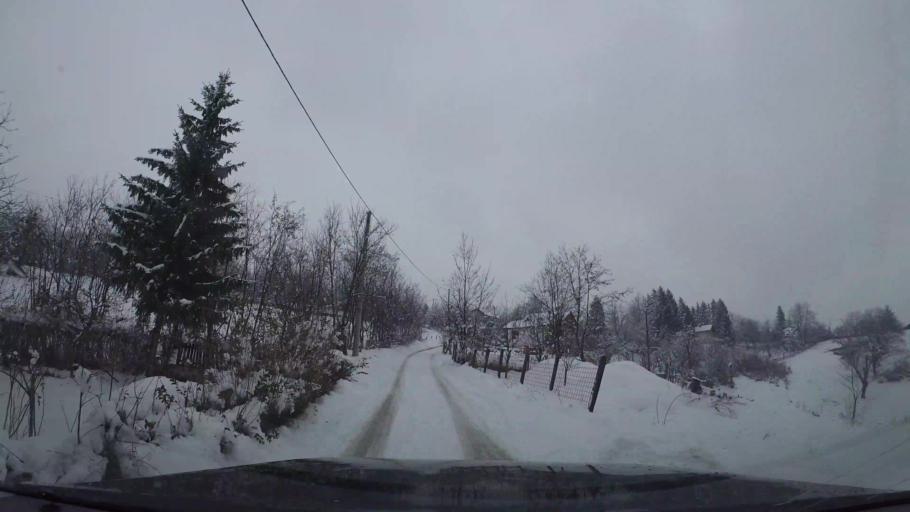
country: BA
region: Federation of Bosnia and Herzegovina
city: Hadzici
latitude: 43.8527
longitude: 18.2572
